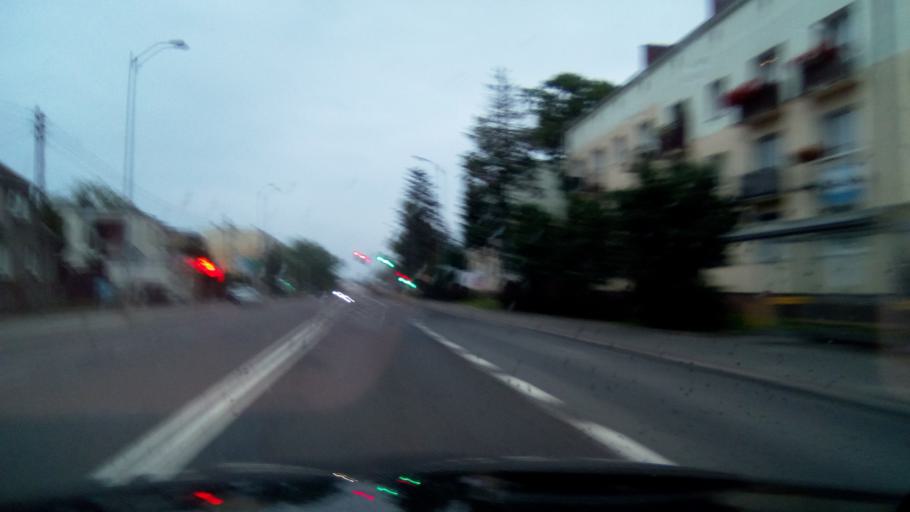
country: PL
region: Greater Poland Voivodeship
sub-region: Powiat poznanski
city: Swarzedz
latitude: 52.4116
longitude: 17.0849
